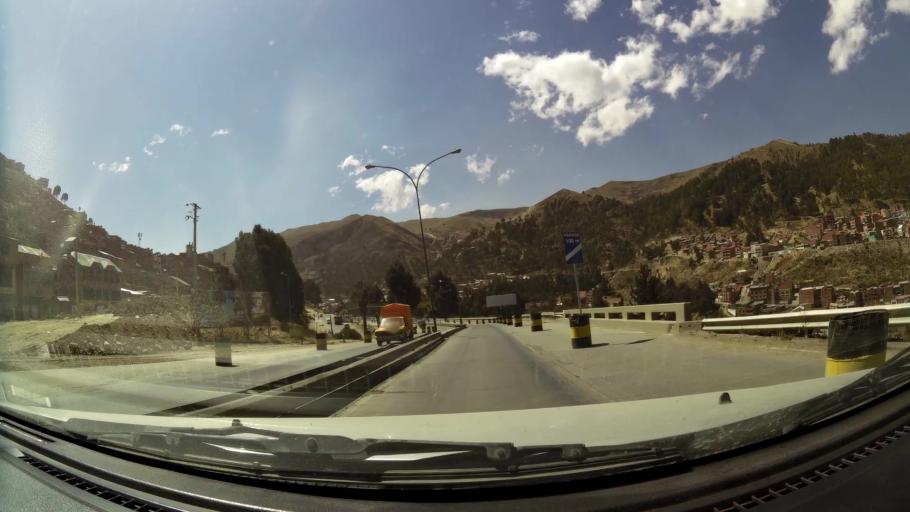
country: BO
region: La Paz
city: La Paz
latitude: -16.4626
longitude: -68.1518
